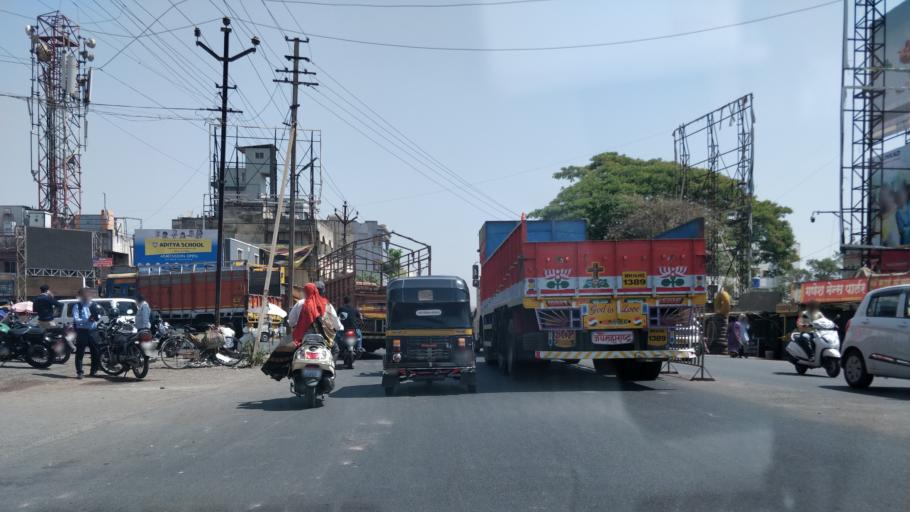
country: IN
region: Maharashtra
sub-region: Pune Division
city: Alandi
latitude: 18.6711
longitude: 73.8916
